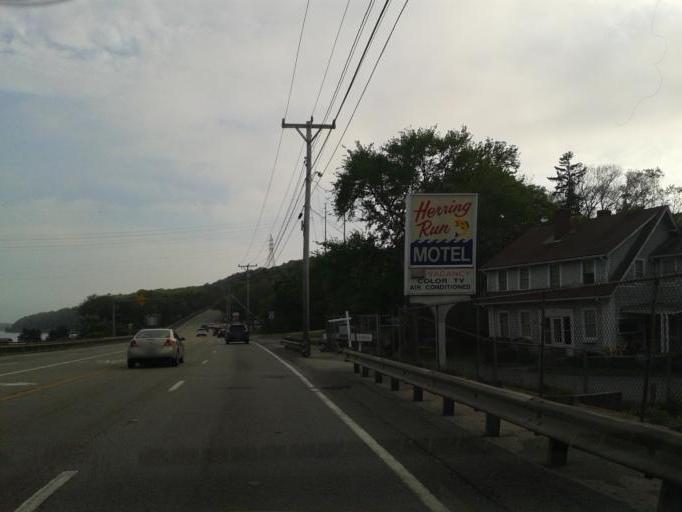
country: US
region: Massachusetts
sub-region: Barnstable County
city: Sagamore
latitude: 41.7730
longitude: -70.5619
